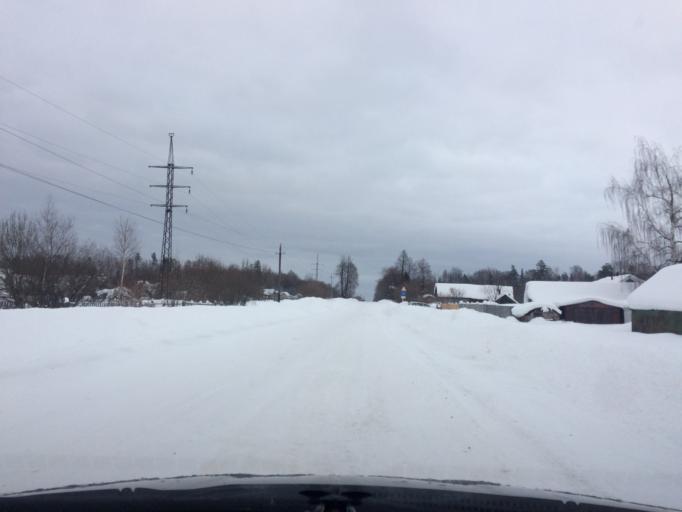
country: RU
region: Mariy-El
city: Mochalishche
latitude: 56.5457
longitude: 48.4073
